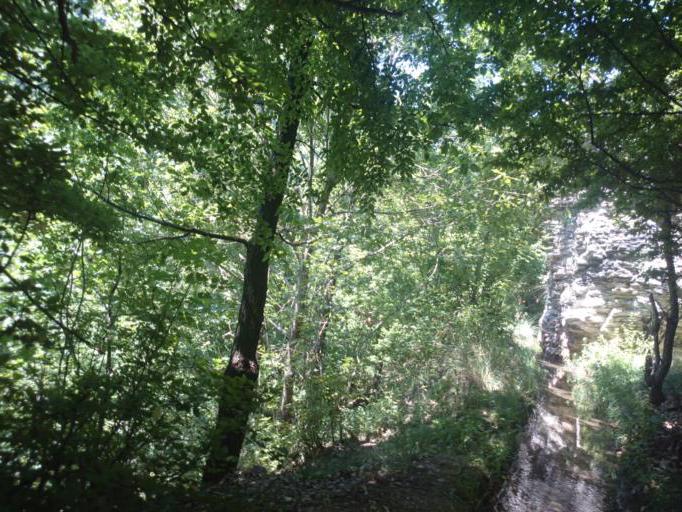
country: AL
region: Diber
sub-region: Rrethi i Dibres
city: Melan
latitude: 41.6181
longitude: 20.4234
